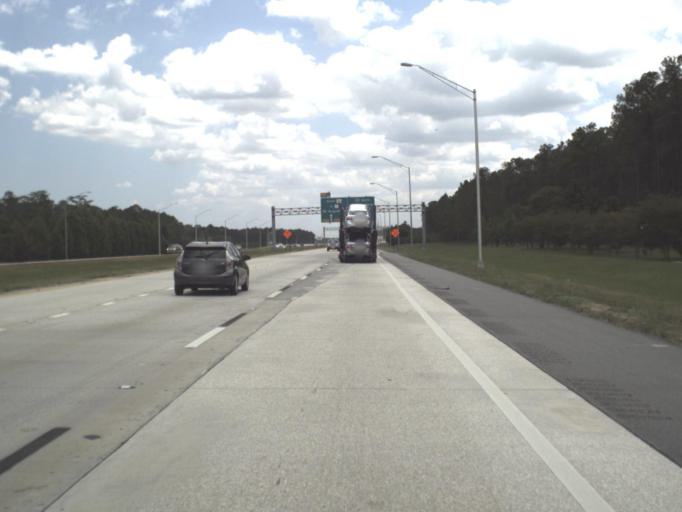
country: US
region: Florida
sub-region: Saint Johns County
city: Palm Valley
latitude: 30.1910
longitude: -81.5139
